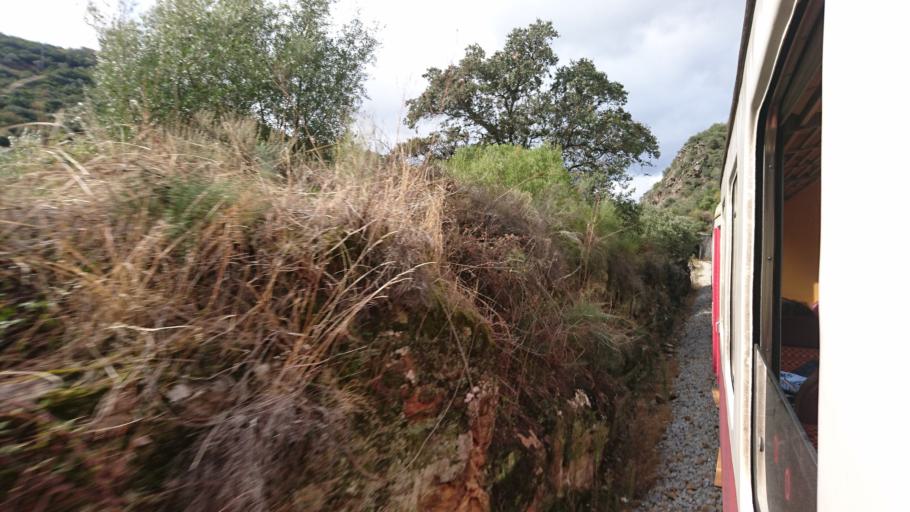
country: PT
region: Viseu
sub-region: Armamar
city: Armamar
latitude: 41.1453
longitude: -7.7145
